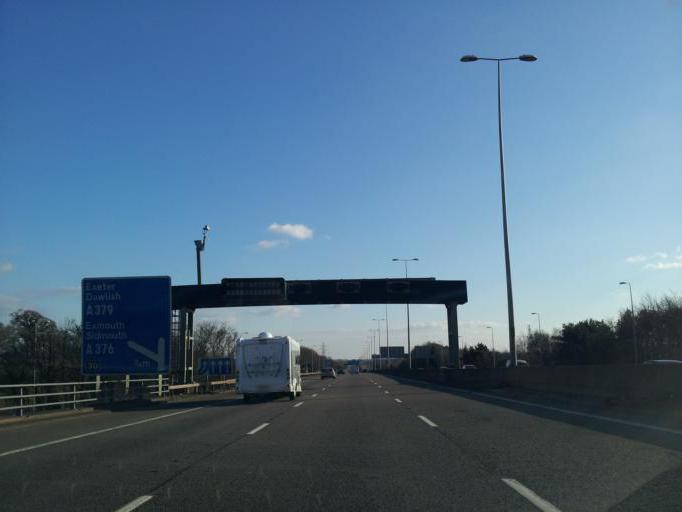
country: GB
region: England
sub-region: Devon
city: Heavitree
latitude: 50.7288
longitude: -3.4623
